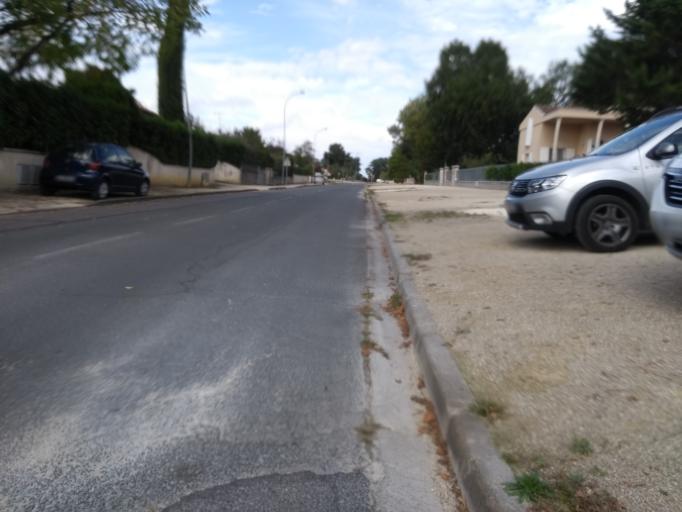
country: FR
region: Aquitaine
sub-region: Departement de la Gironde
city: Canejan
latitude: 44.7649
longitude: -0.6594
